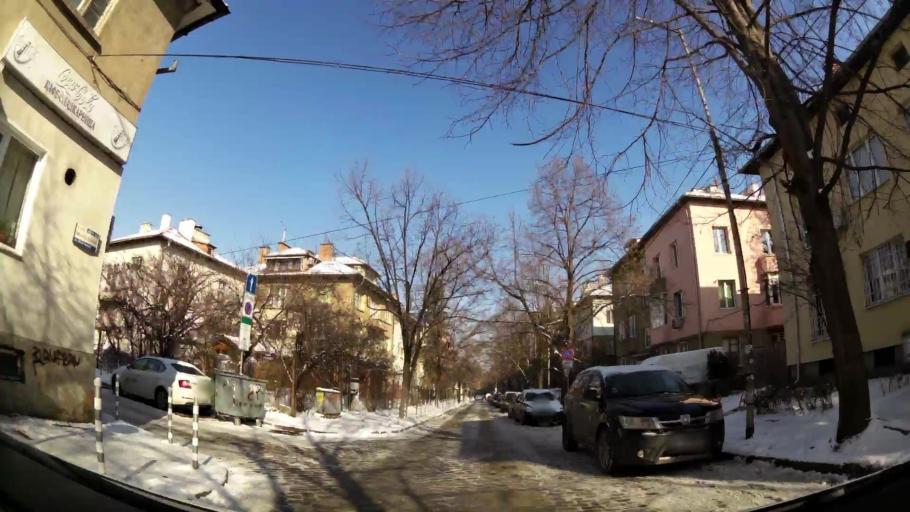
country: BG
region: Sofia-Capital
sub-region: Stolichna Obshtina
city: Sofia
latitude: 42.6798
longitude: 23.3276
